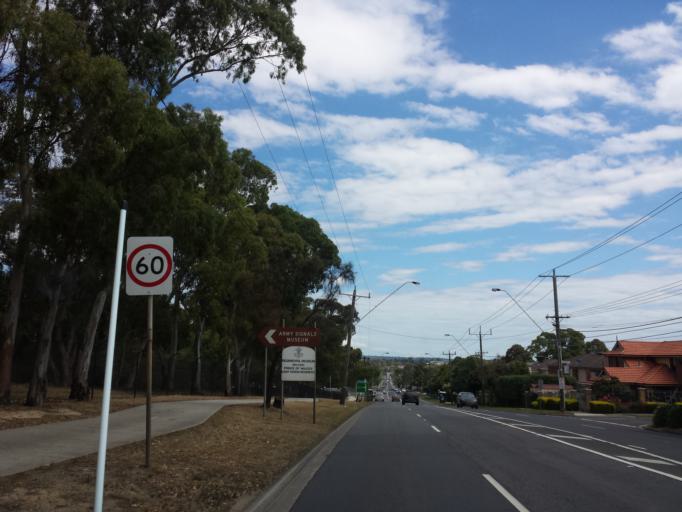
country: AU
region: Victoria
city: Watsonia
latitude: -37.7203
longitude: 145.0811
